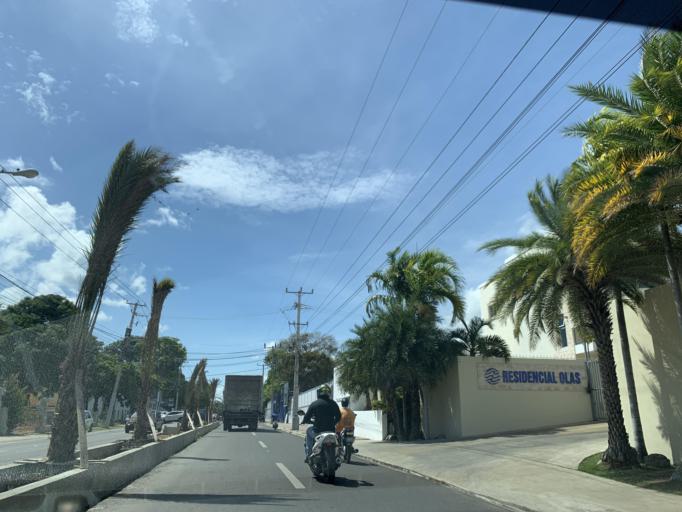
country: DO
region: Puerto Plata
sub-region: Puerto Plata
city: Puerto Plata
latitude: 19.7906
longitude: -70.6803
